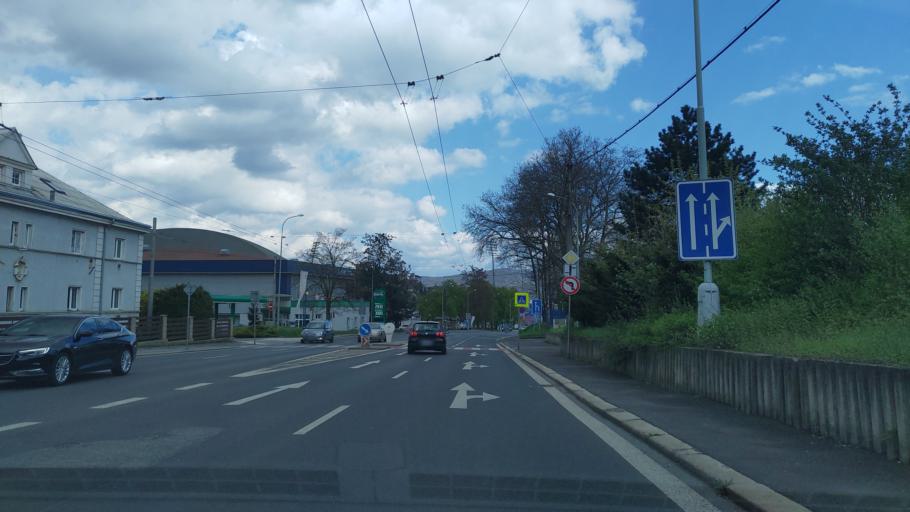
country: CZ
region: Ustecky
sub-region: Okres Usti nad Labem
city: Usti nad Labem
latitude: 50.6780
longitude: 14.0112
